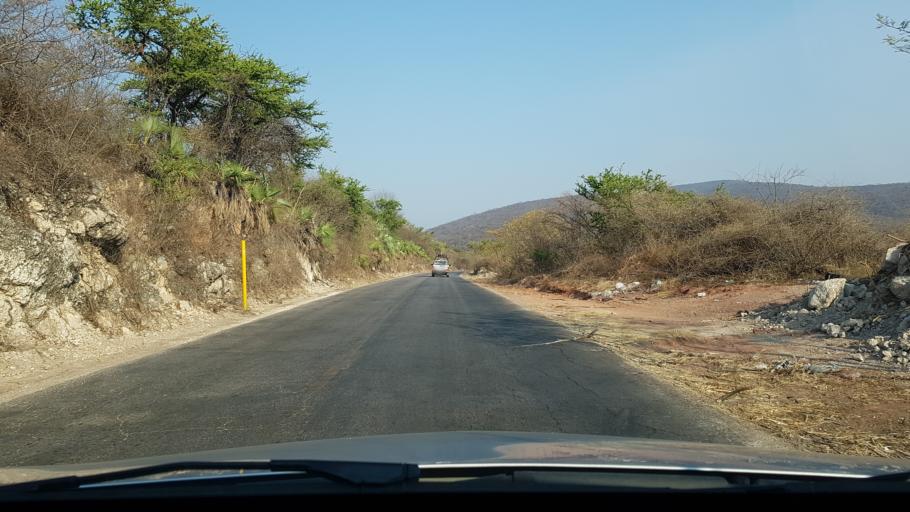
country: MX
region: Morelos
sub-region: Tlaltizapan de Zapata
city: Colonia Palo Prieto (Chipitongo)
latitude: 18.6733
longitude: -99.0591
